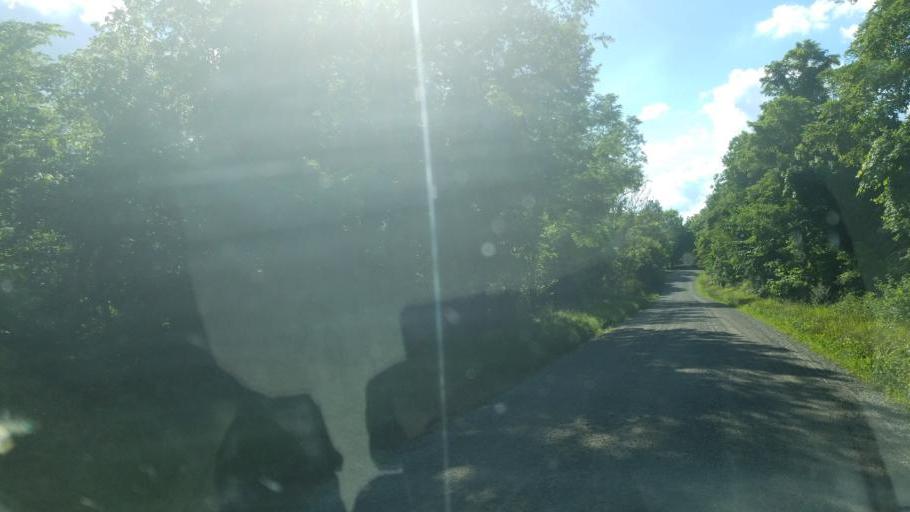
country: US
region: Ohio
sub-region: Gallia County
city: Gallipolis
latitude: 38.7450
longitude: -82.3488
